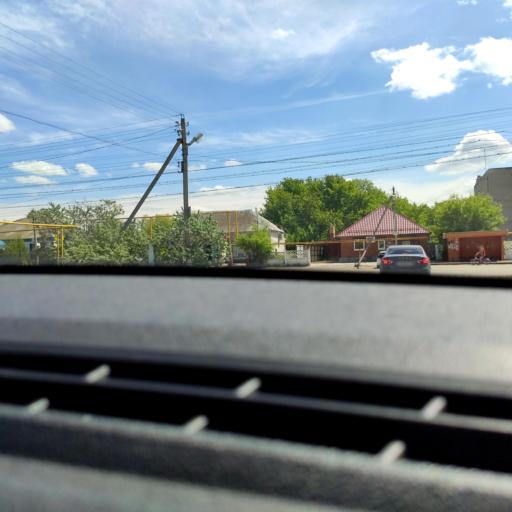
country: RU
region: Samara
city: Povolzhskiy
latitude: 53.6437
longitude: 49.6916
